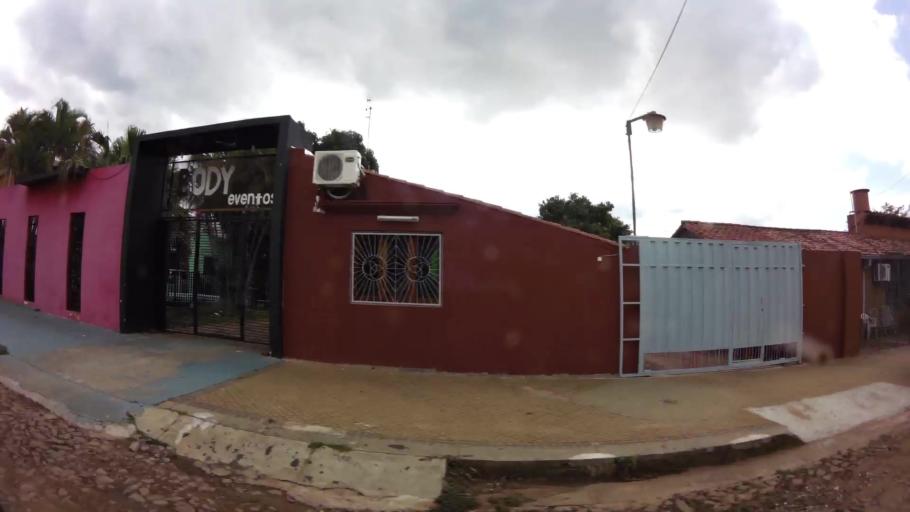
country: PY
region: Central
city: San Lorenzo
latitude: -25.2717
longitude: -57.5048
